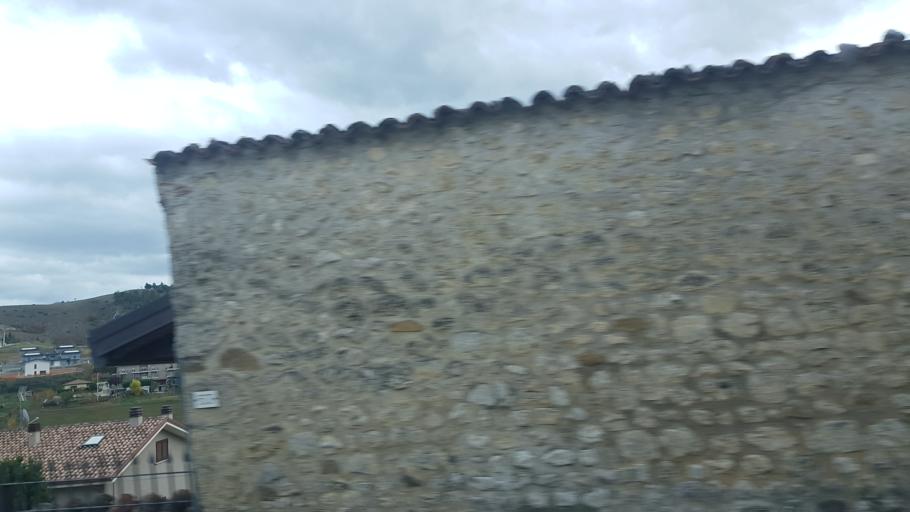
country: IT
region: Abruzzo
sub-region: Provincia dell' Aquila
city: Progetto Case Bazzano
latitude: 42.3548
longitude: 13.4254
